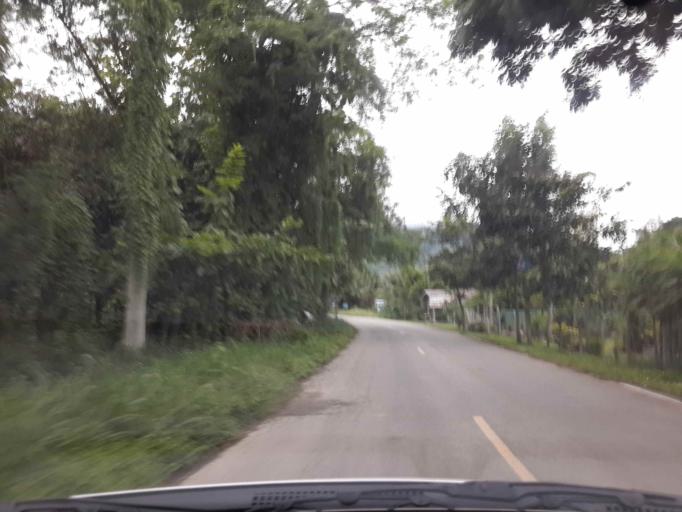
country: TH
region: Ratchaburi
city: Suan Phueng
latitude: 13.5864
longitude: 99.2251
